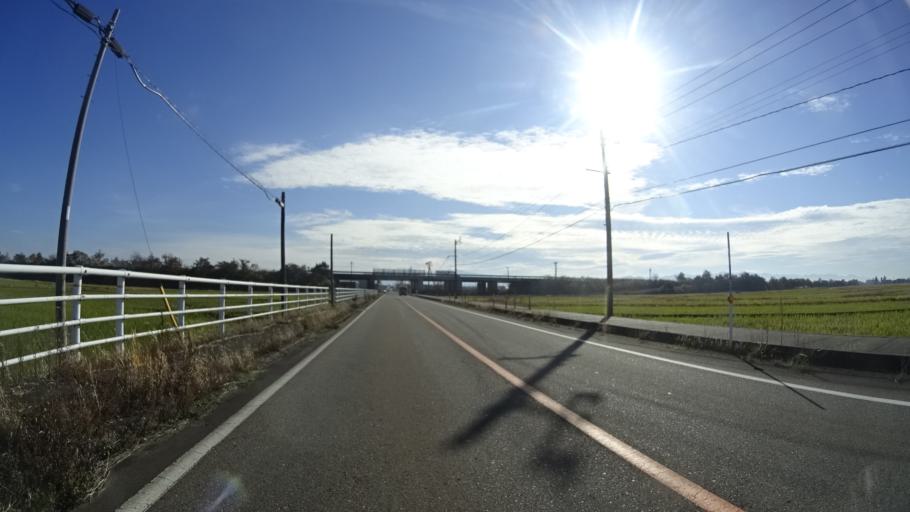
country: JP
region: Niigata
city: Mitsuke
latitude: 37.5501
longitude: 138.8707
